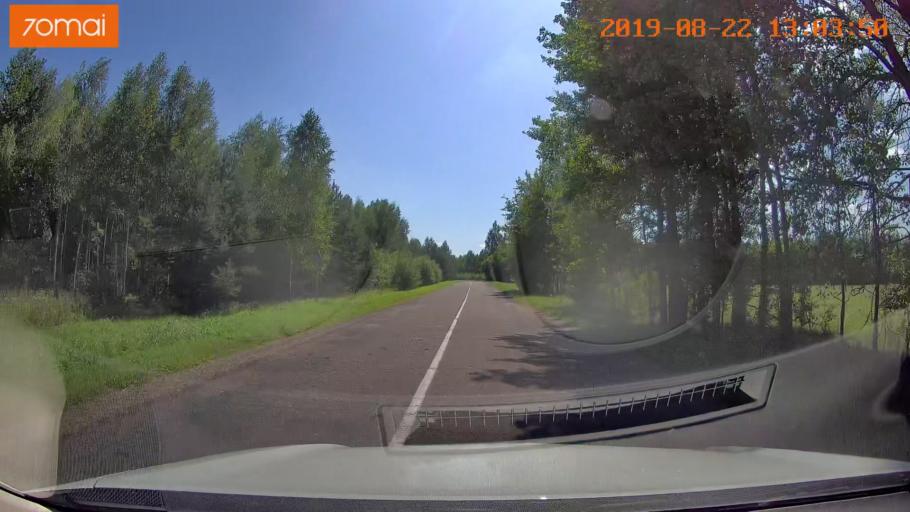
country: BY
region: Minsk
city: Prawdzinski
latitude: 53.3769
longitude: 27.8213
